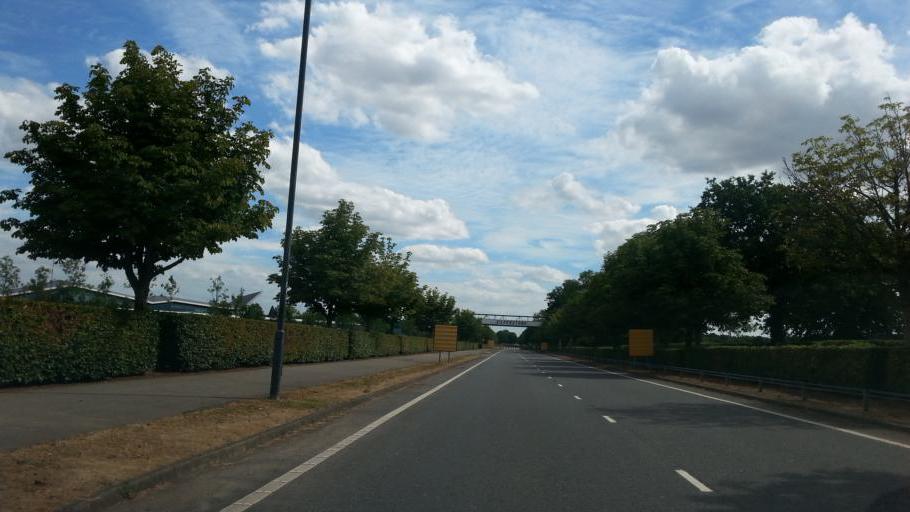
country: GB
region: England
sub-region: Northamptonshire
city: Silverstone
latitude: 52.0729
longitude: -1.0257
